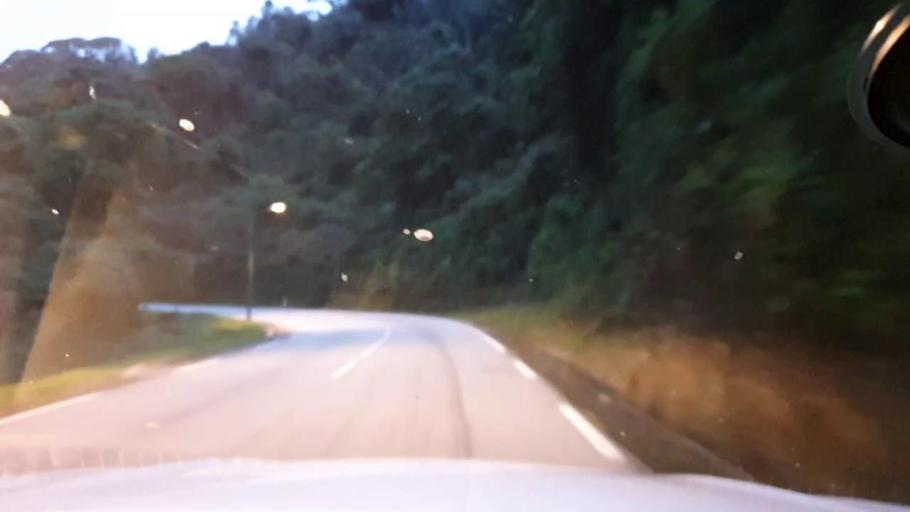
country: RW
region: Southern Province
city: Nzega
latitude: -2.5278
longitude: 29.3754
